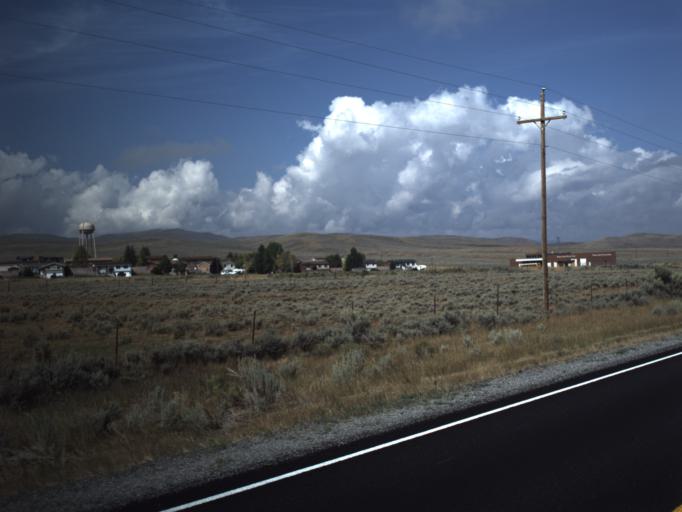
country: US
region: Utah
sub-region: Rich County
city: Randolph
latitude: 41.5844
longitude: -111.1677
